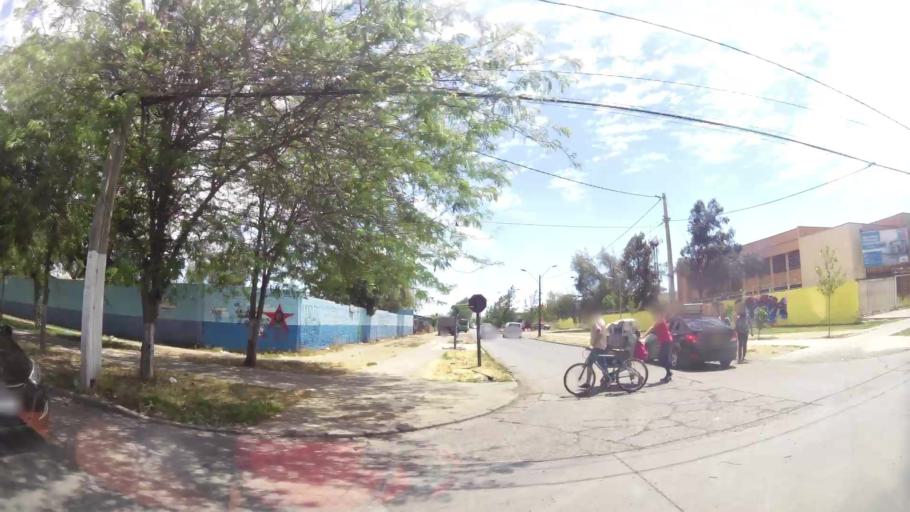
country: CL
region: Santiago Metropolitan
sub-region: Provincia de Santiago
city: La Pintana
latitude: -33.5513
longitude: -70.6445
